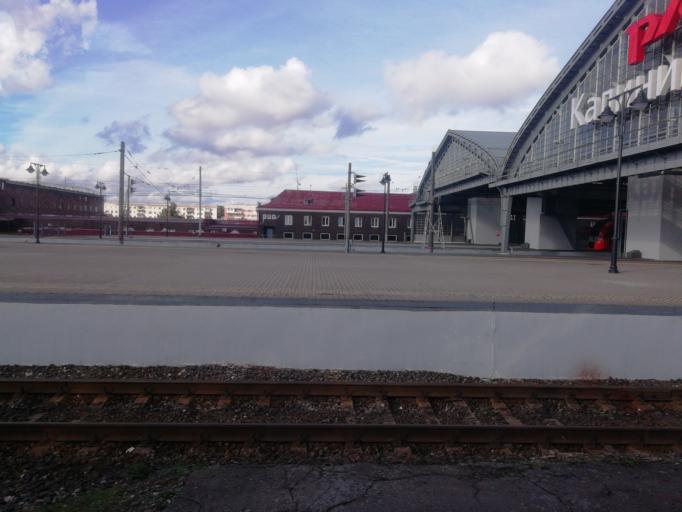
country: RU
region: Kaliningrad
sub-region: Gorod Kaliningrad
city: Kaliningrad
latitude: 54.6939
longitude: 20.4970
